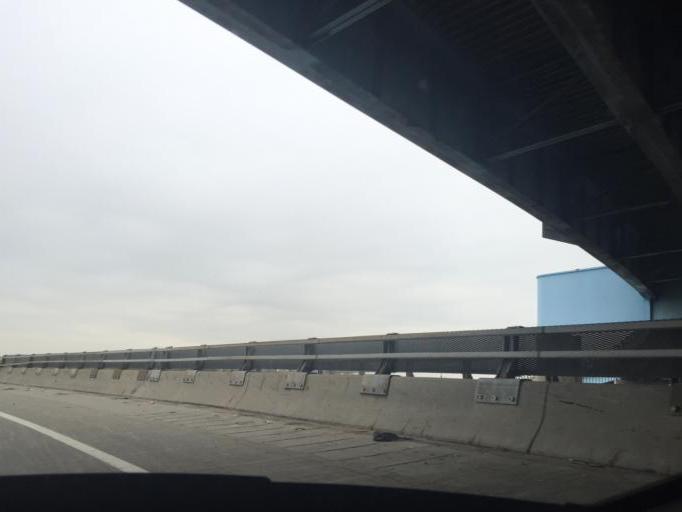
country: US
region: Michigan
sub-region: Wayne County
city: Dearborn
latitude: 42.3788
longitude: -83.2170
